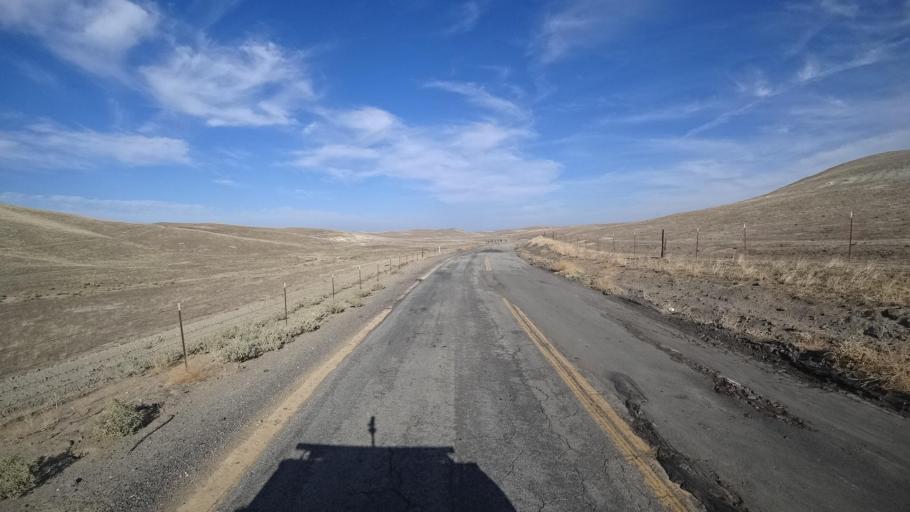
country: US
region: California
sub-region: Kern County
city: Oildale
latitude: 35.6183
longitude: -118.9870
